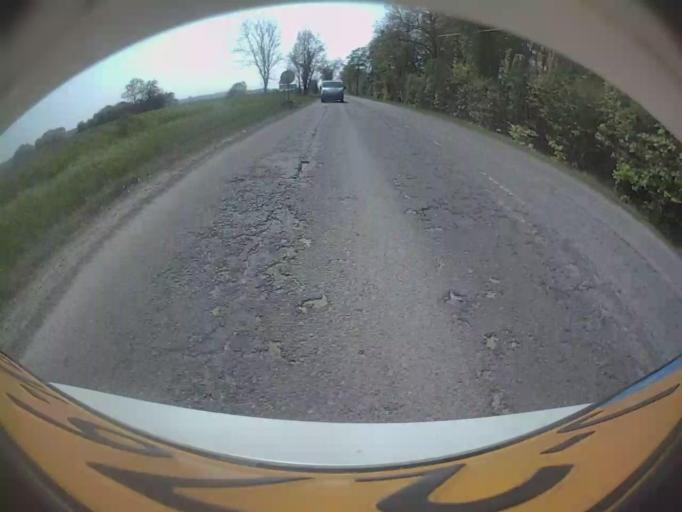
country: BE
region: Wallonia
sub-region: Province de Namur
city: Houyet
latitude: 50.2633
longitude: 5.0228
